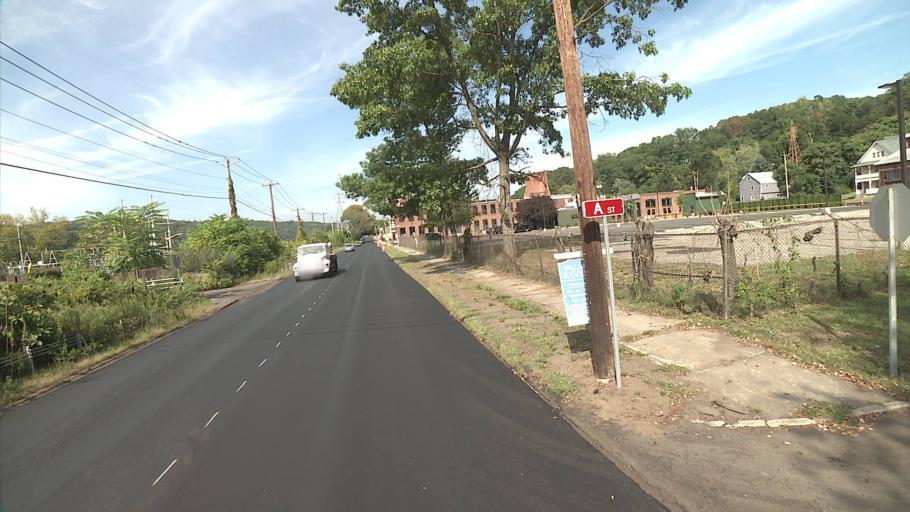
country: US
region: Connecticut
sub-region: Fairfield County
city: Shelton
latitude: 41.3255
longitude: -73.0984
